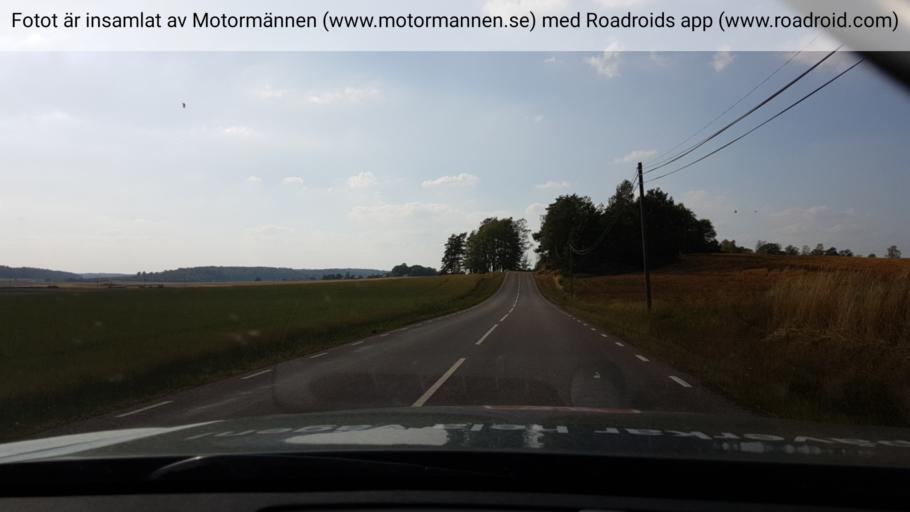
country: SE
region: Soedermanland
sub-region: Gnesta Kommun
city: Gnesta
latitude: 59.0980
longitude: 17.2371
